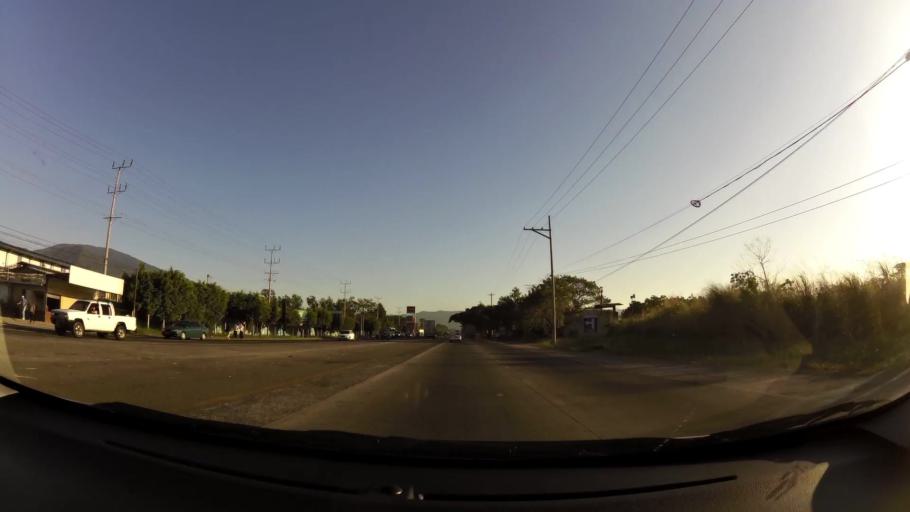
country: SV
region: La Libertad
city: Ciudad Arce
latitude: 13.7762
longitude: -89.3728
